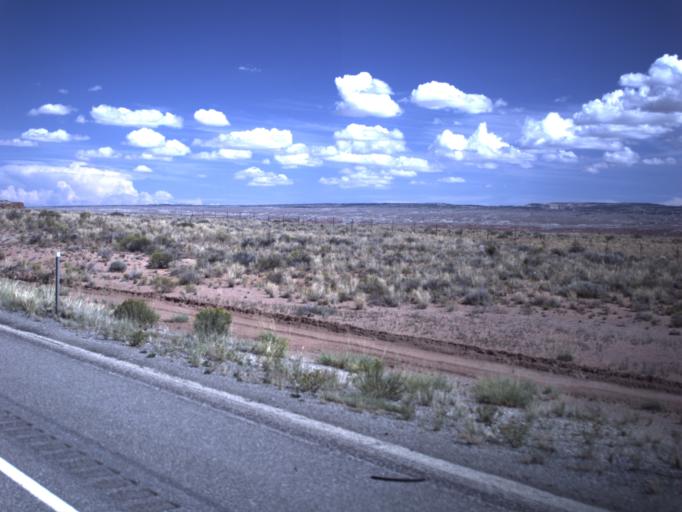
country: US
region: Utah
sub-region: Emery County
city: Ferron
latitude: 38.8352
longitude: -111.1027
